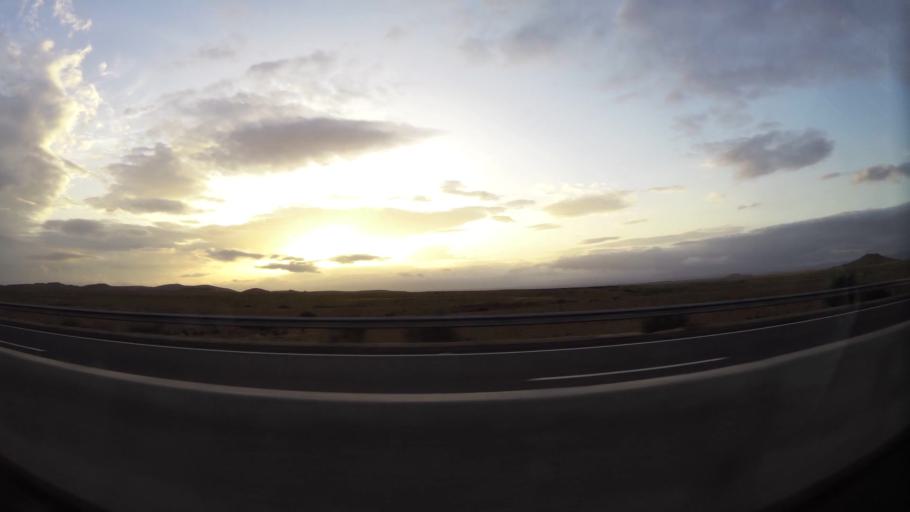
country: MA
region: Oriental
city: Taourirt
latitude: 34.5203
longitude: -2.9367
